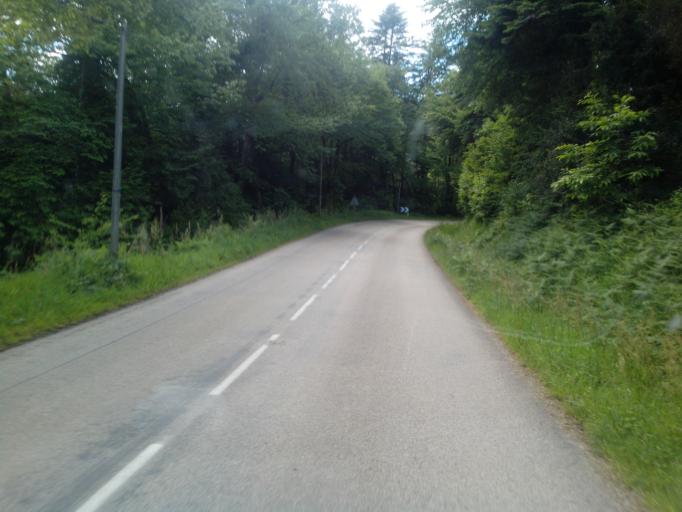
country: FR
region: Brittany
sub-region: Departement du Finistere
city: Berrien
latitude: 48.3927
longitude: -3.7244
